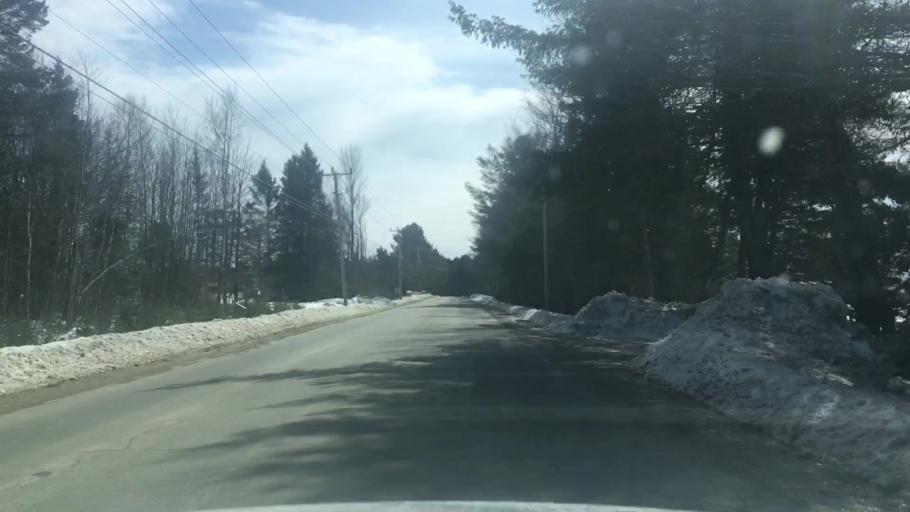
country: US
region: Maine
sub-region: Penobscot County
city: Holden
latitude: 44.7691
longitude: -68.6482
